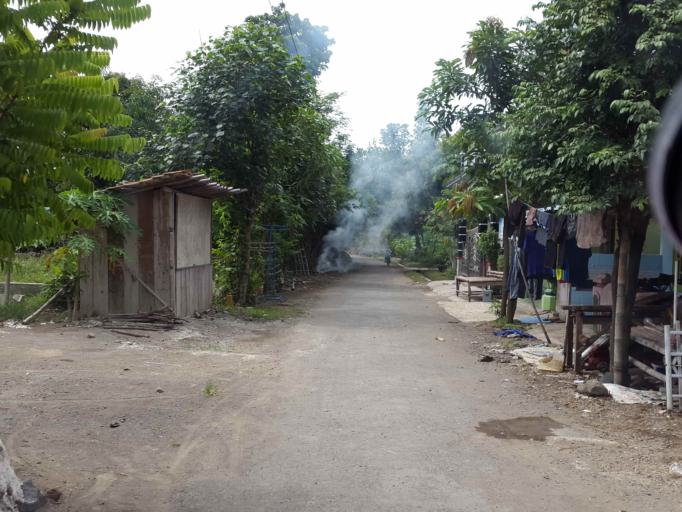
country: ID
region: Central Java
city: Pemalang
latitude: -6.8673
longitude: 109.3687
